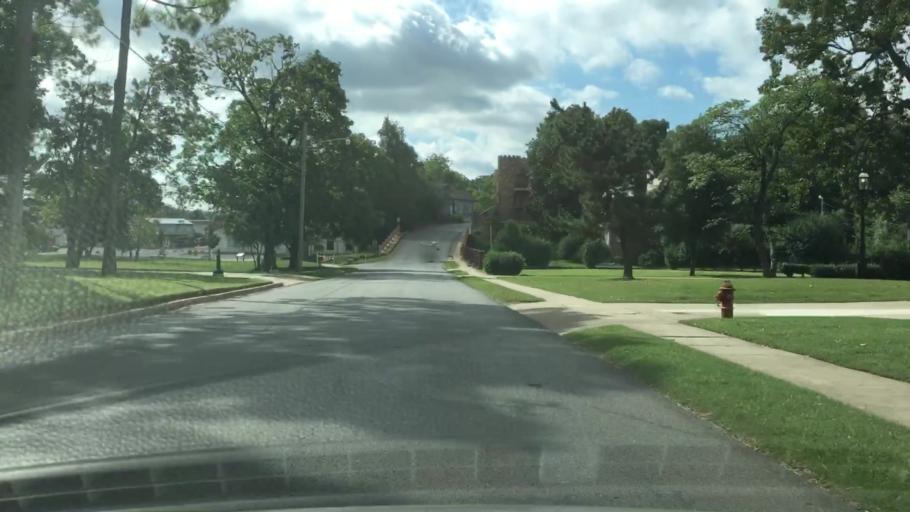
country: US
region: Oklahoma
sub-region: Cherokee County
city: Tahlequah
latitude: 35.9190
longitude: -94.9705
